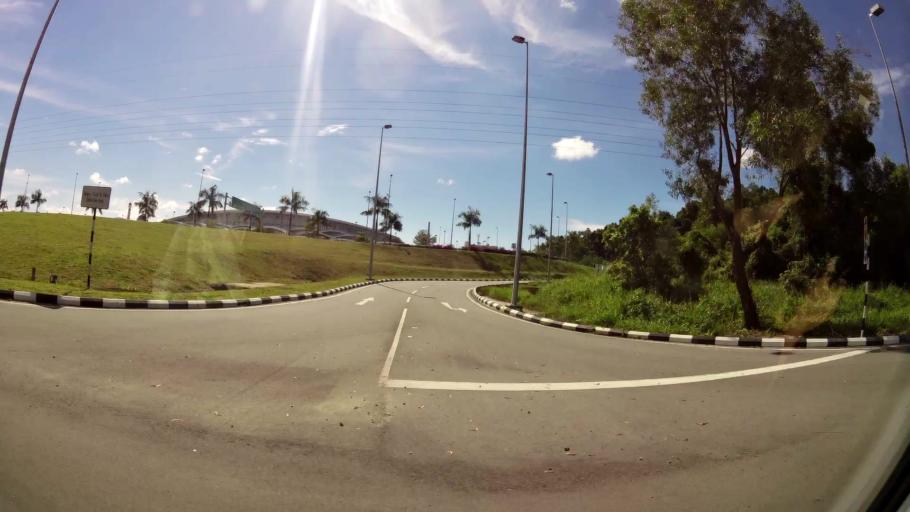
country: BN
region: Brunei and Muara
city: Bandar Seri Begawan
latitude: 4.9444
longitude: 114.9369
